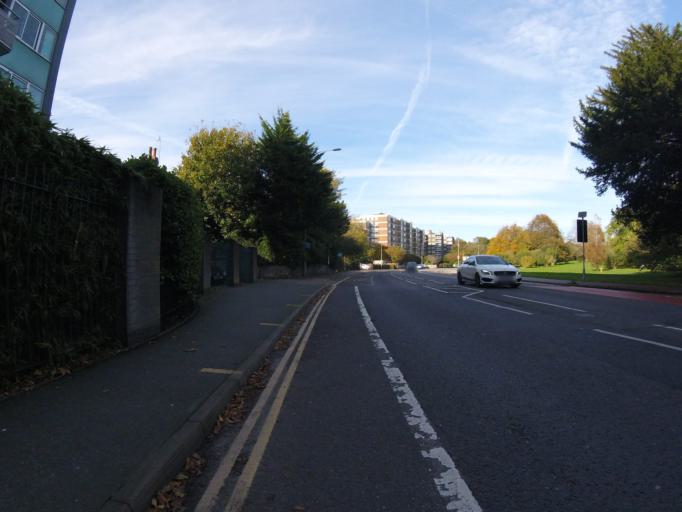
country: GB
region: England
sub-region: Brighton and Hove
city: Hove
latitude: 50.8530
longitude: -0.1548
